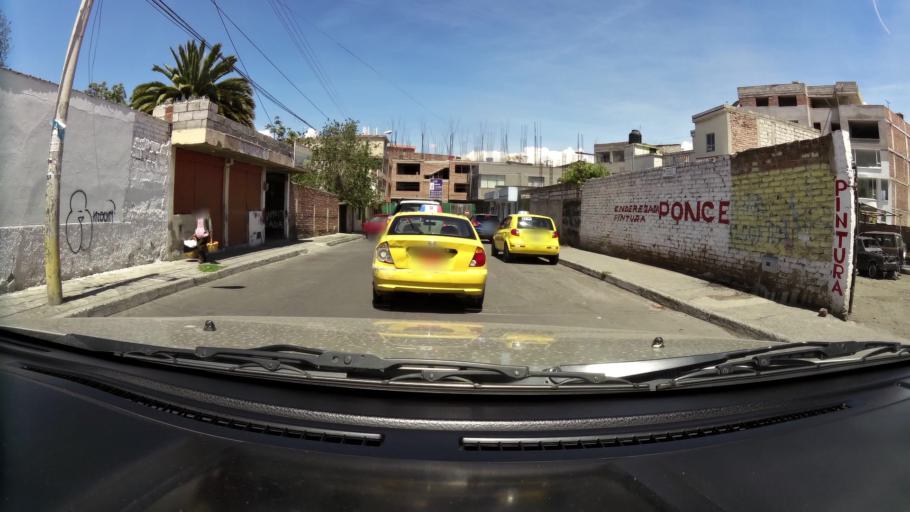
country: EC
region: Chimborazo
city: Riobamba
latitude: -1.6692
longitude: -78.6574
